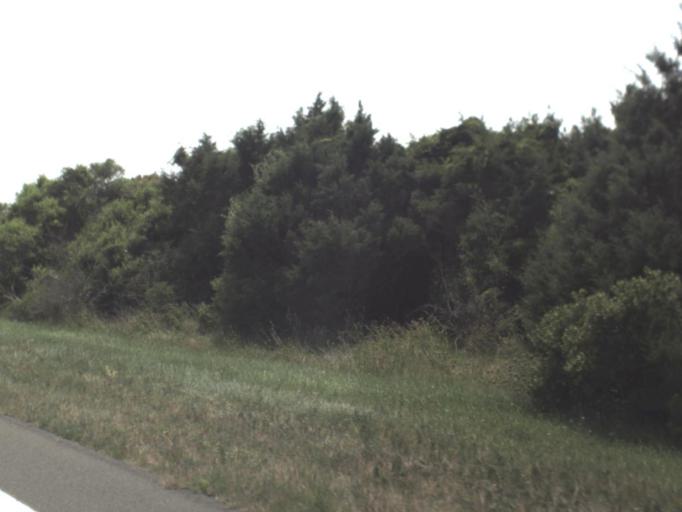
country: US
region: Florida
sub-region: Duval County
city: Atlantic Beach
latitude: 30.4424
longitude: -81.4155
